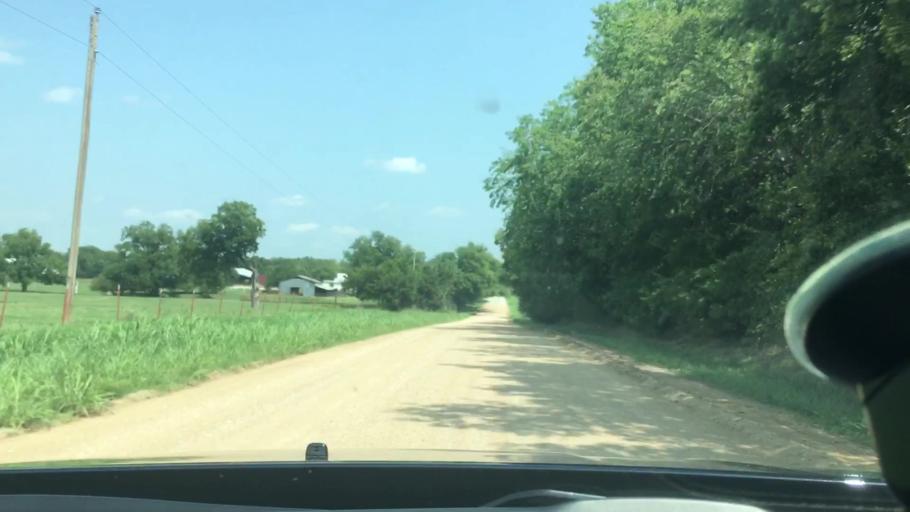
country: US
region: Oklahoma
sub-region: Coal County
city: Coalgate
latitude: 34.4330
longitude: -96.4387
